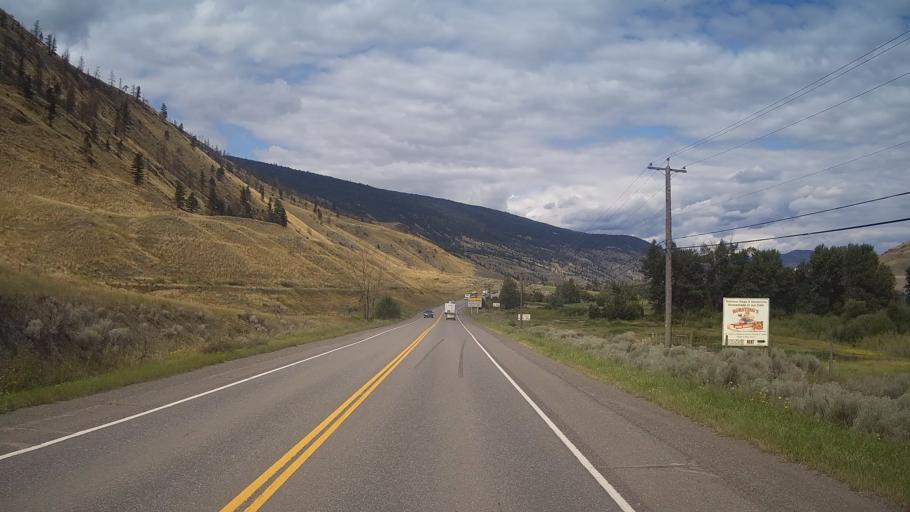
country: CA
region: British Columbia
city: Cache Creek
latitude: 50.8246
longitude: -121.3474
